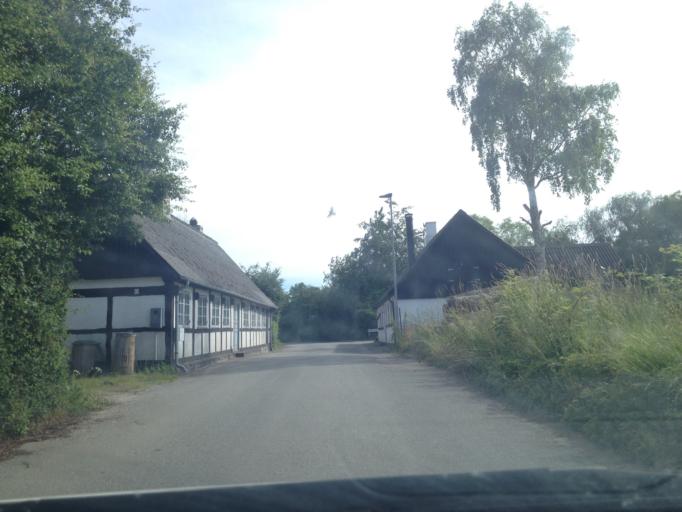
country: DK
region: Central Jutland
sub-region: Samso Kommune
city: Tranebjerg
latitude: 55.7949
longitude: 10.5554
